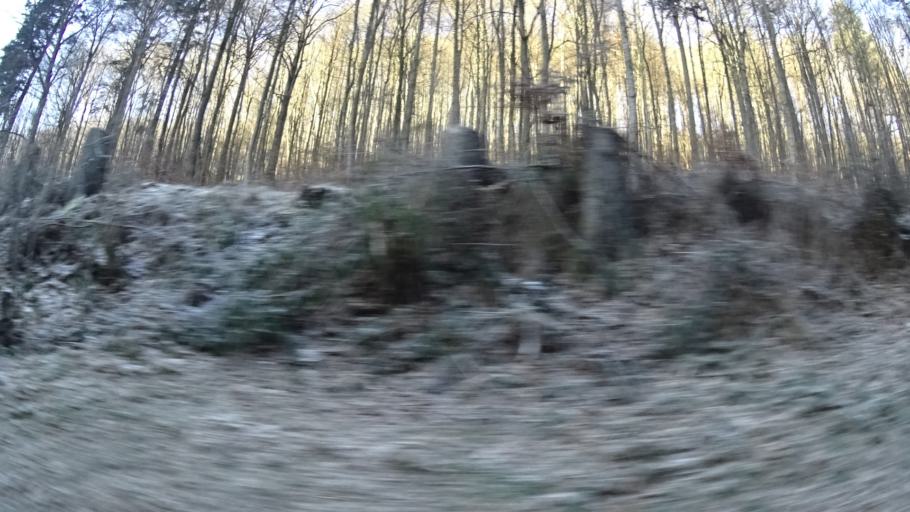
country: DE
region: Thuringia
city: Judenbach
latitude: 50.3694
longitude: 11.2155
